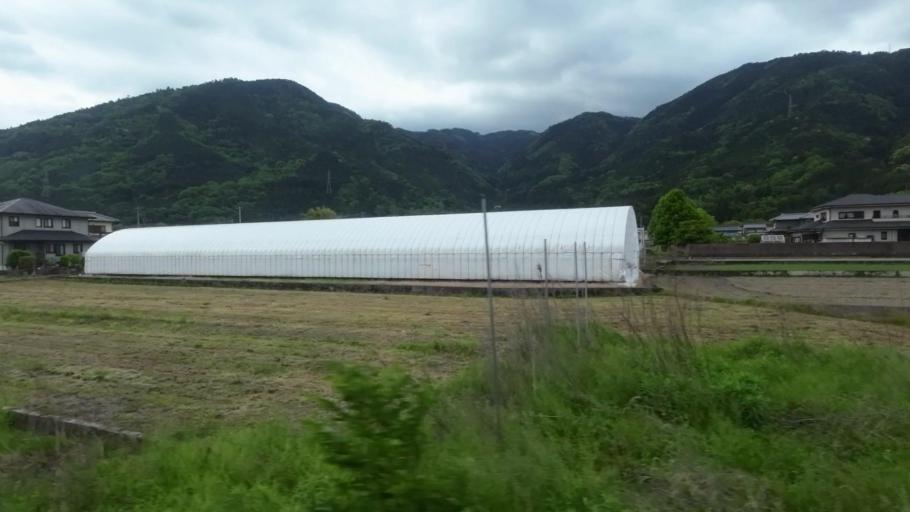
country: JP
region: Tokushima
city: Ikedacho
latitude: 34.0355
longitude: 133.9146
